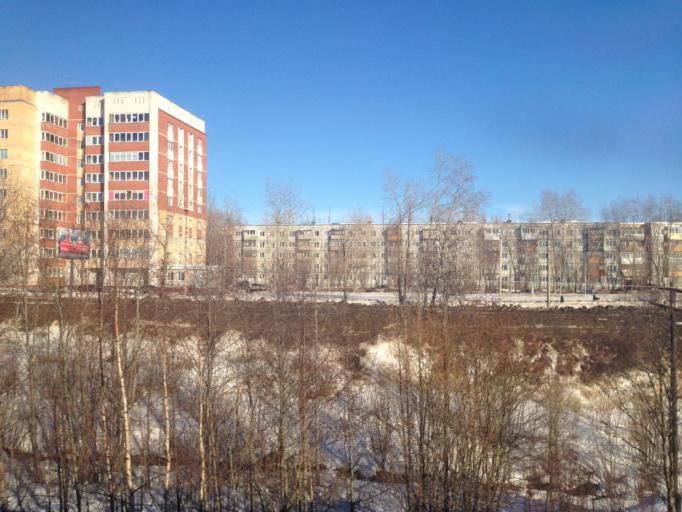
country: RU
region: Komi Republic
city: Ezhva
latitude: 61.7938
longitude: 50.7385
